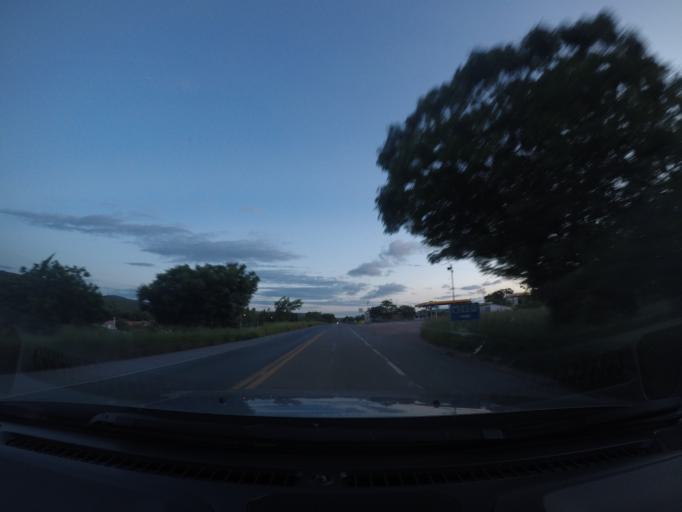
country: BR
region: Bahia
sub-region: Seabra
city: Seabra
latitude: -12.4712
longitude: -41.7422
